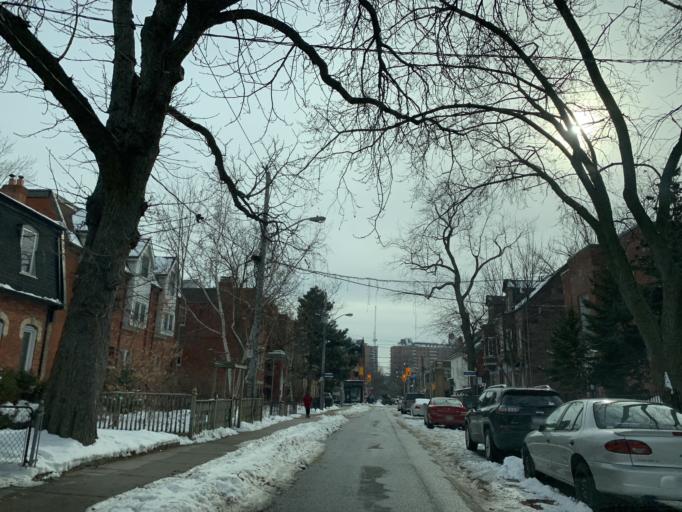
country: CA
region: Ontario
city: Toronto
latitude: 43.6598
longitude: -79.3689
